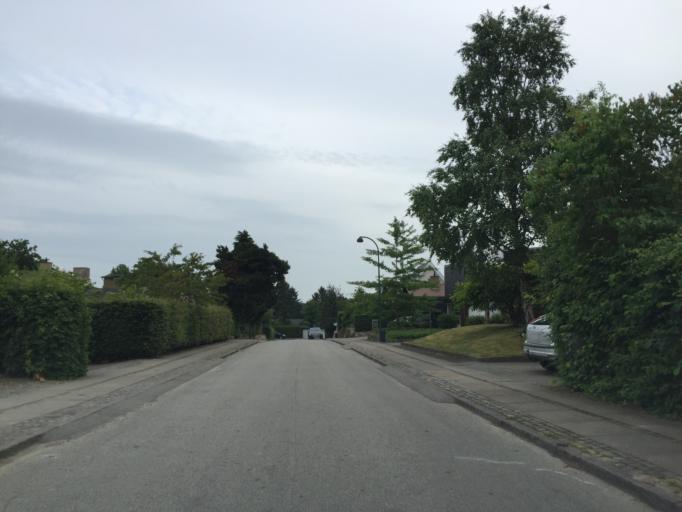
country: DK
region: Capital Region
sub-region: Lyngby-Tarbaek Kommune
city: Kongens Lyngby
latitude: 55.7665
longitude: 12.5296
